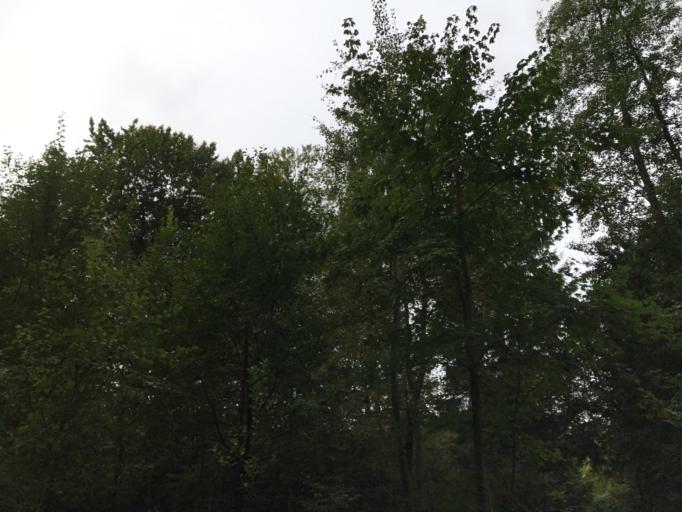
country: DE
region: Bavaria
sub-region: Upper Bavaria
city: Grunwald
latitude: 48.0216
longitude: 11.5337
